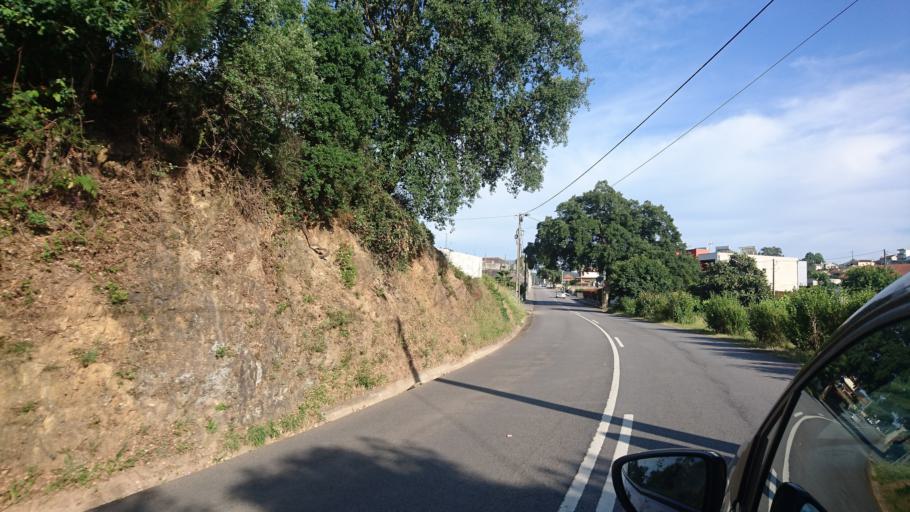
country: PT
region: Porto
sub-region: Paredes
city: Recarei
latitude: 41.1276
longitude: -8.3733
